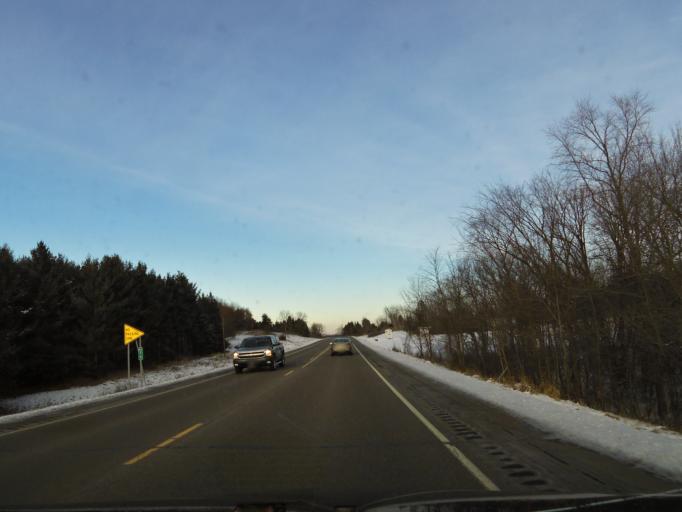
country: US
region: Minnesota
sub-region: Chisago County
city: Shafer
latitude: 45.3717
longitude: -92.7080
